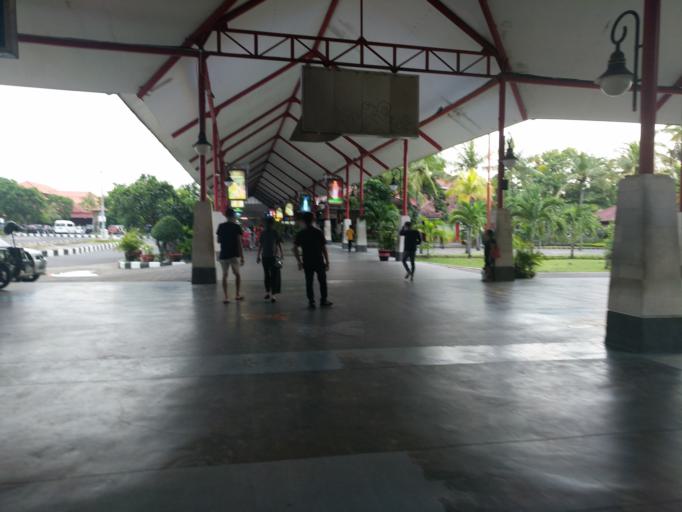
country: ID
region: Bali
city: Kelanabian
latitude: -8.7429
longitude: 115.1639
